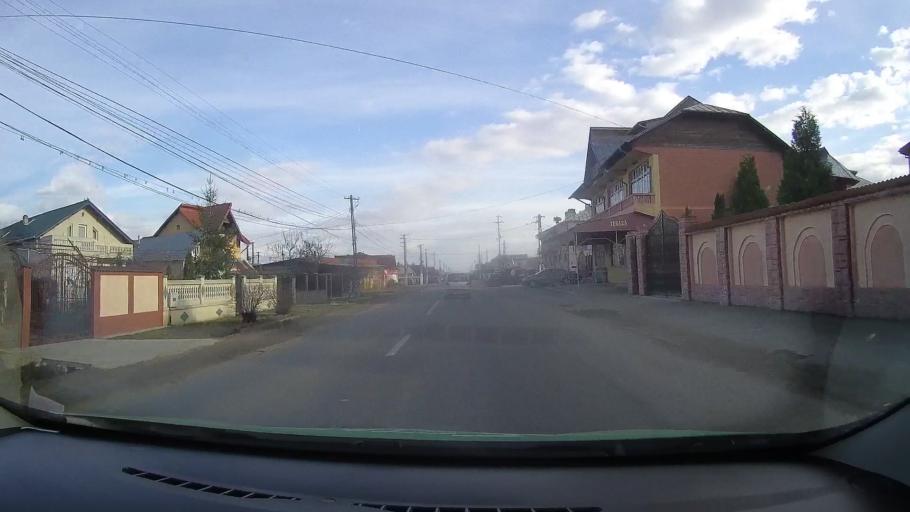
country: RO
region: Dambovita
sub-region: Comuna Vacaresti
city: Vacaresti
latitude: 44.8573
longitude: 25.4841
